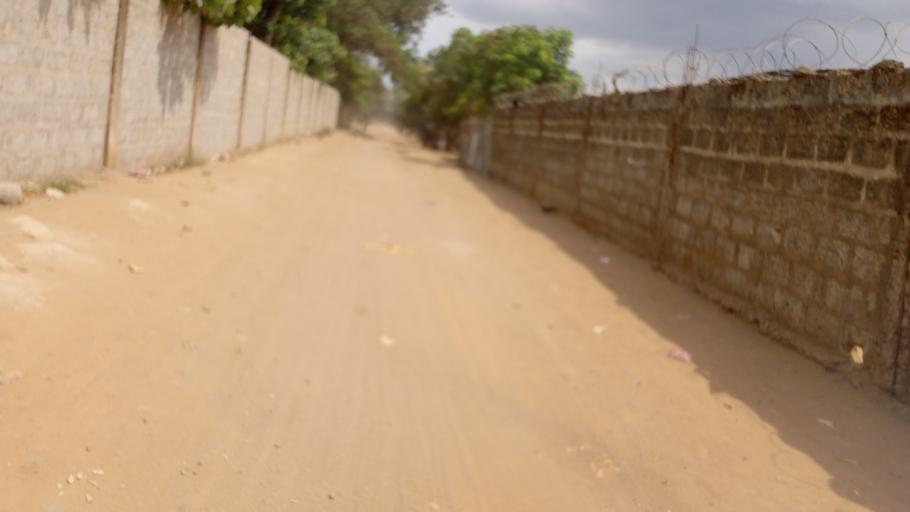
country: SL
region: Western Area
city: Waterloo
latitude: 8.3191
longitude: -13.0649
